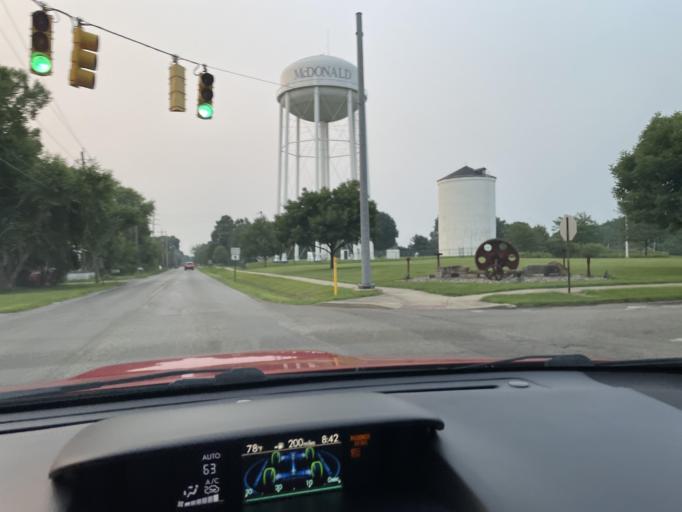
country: US
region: Ohio
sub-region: Trumbull County
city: McDonald
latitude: 41.1601
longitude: -80.7328
